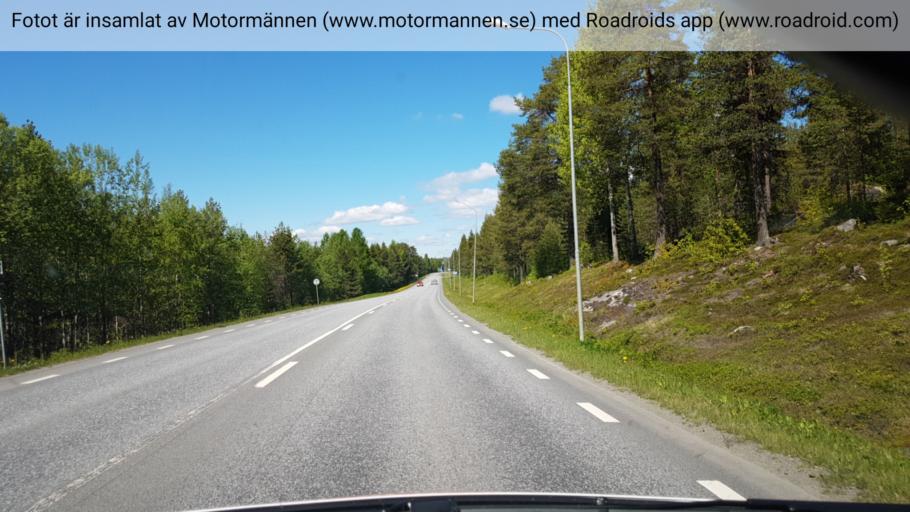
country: SE
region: Vaesterbotten
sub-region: Vilhelmina Kommun
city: Vilhelmina
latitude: 64.6357
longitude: 16.6199
